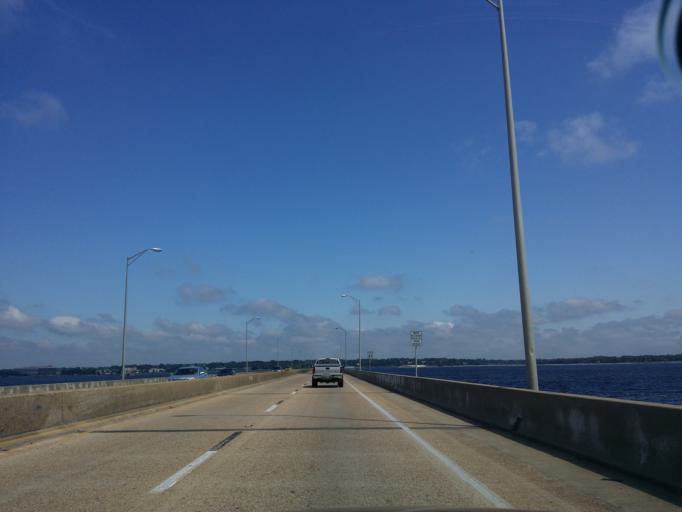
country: US
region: Florida
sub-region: Escambia County
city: East Pensacola Heights
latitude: 30.4003
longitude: -87.1871
